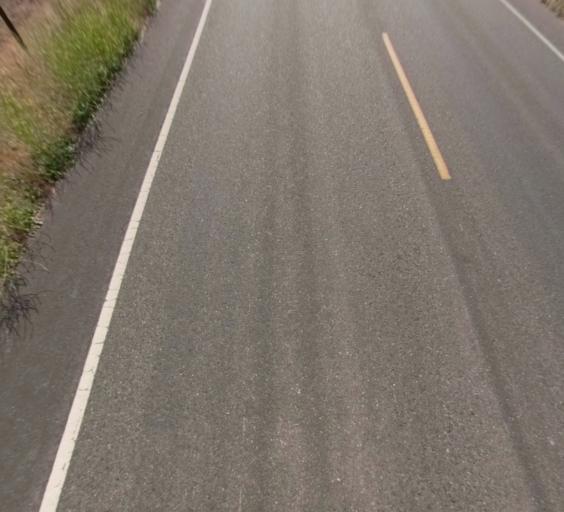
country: US
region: California
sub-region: Madera County
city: Bonadelle Ranchos-Madera Ranchos
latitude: 36.9666
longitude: -119.9462
